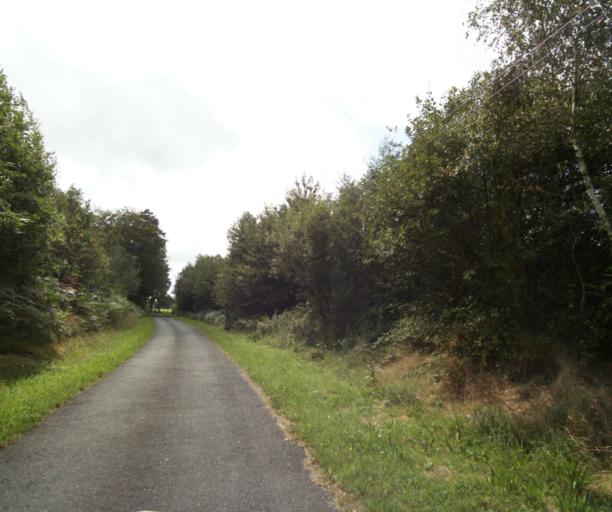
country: FR
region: Limousin
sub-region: Departement de la Correze
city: Sainte-Fortunade
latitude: 45.2042
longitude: 1.8114
